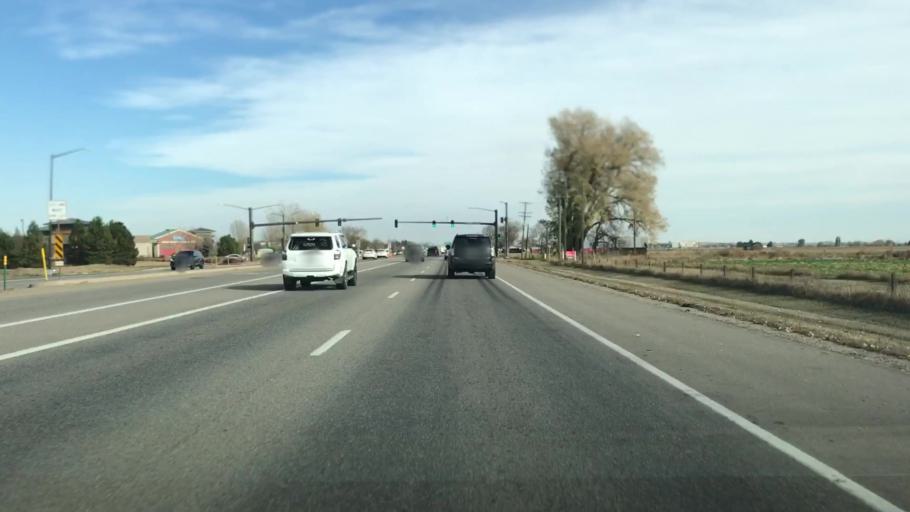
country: US
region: Colorado
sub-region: Larimer County
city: Loveland
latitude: 40.4071
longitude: -105.0132
